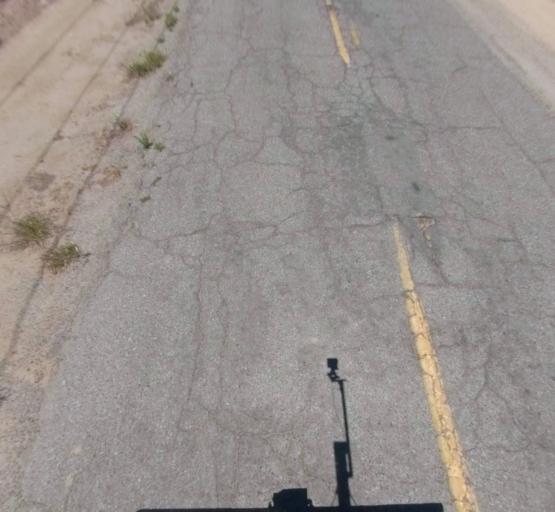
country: US
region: California
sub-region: Madera County
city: Chowchilla
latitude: 37.0544
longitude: -120.3317
